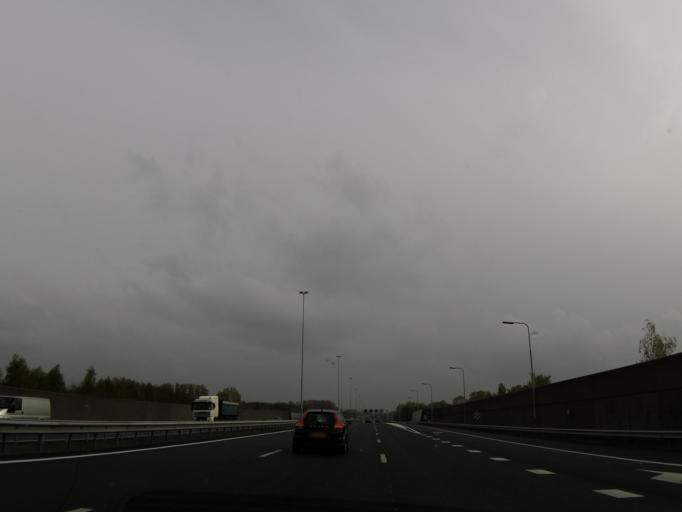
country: NL
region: North Brabant
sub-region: Gemeente Boxtel
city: Boxtel
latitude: 51.5794
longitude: 5.3561
